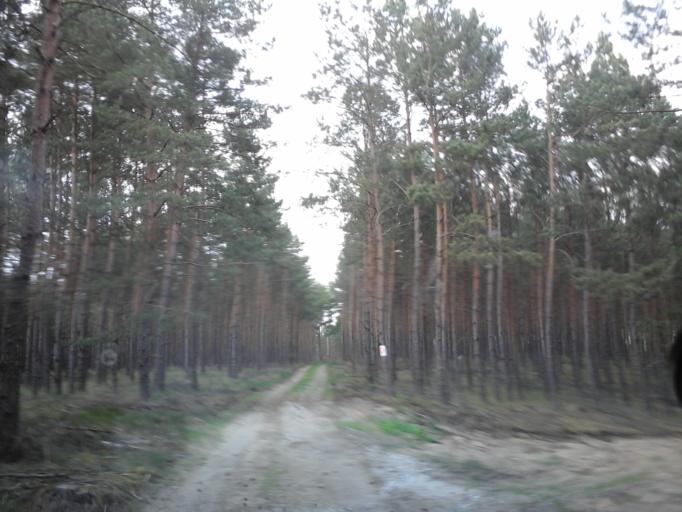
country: PL
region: West Pomeranian Voivodeship
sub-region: Powiat choszczenski
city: Drawno
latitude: 53.1463
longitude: 15.7857
